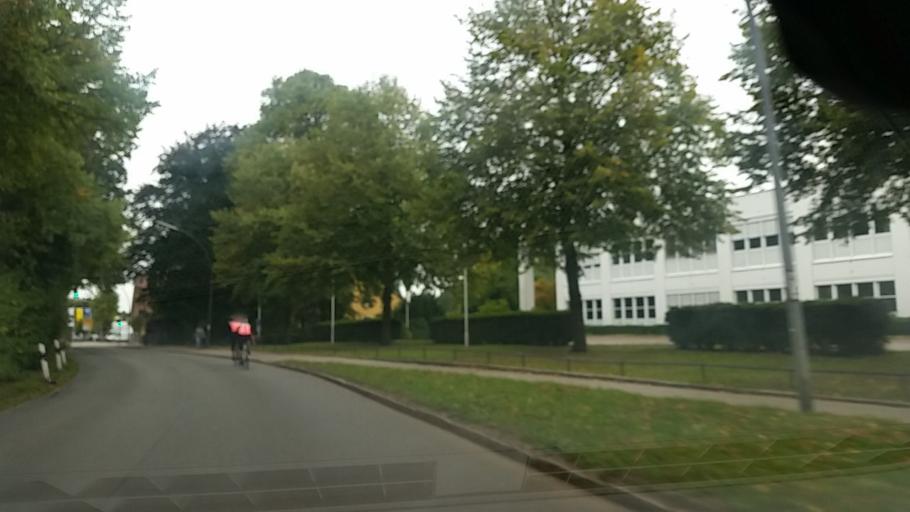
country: DE
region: Hamburg
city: Hummelsbuettel
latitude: 53.6876
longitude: 10.0461
